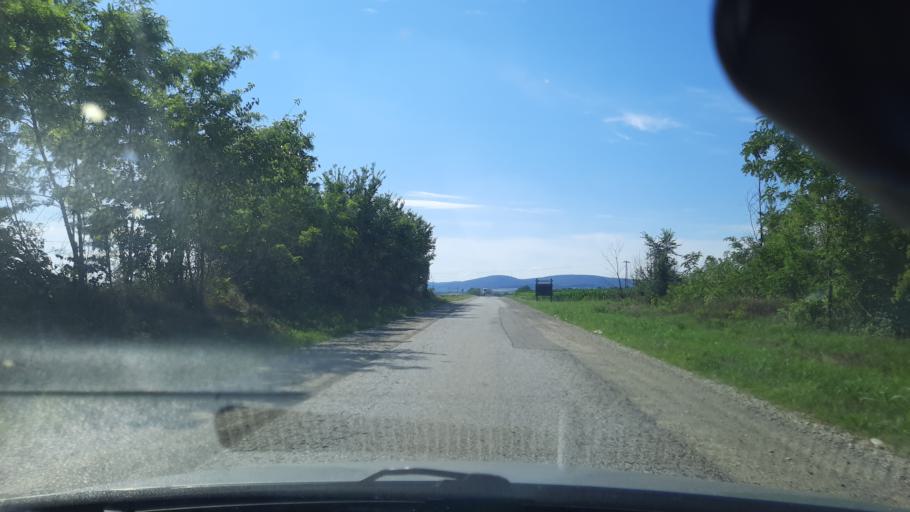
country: RS
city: Cortanovci
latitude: 45.1095
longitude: 19.9752
